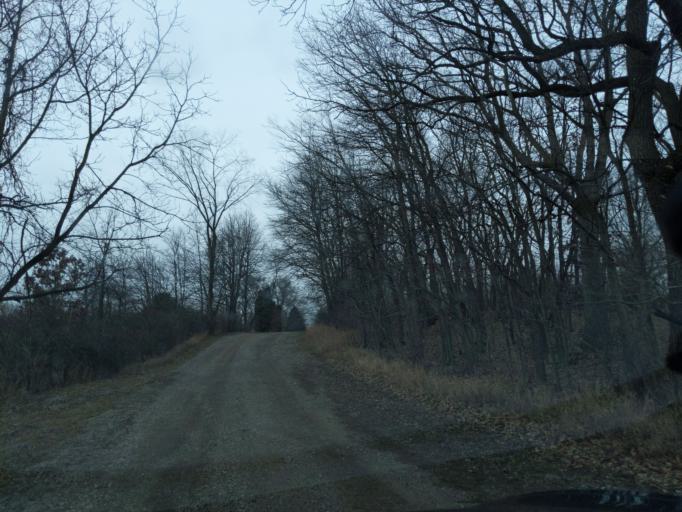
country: US
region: Michigan
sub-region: Ionia County
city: Portland
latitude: 42.9783
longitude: -84.9420
